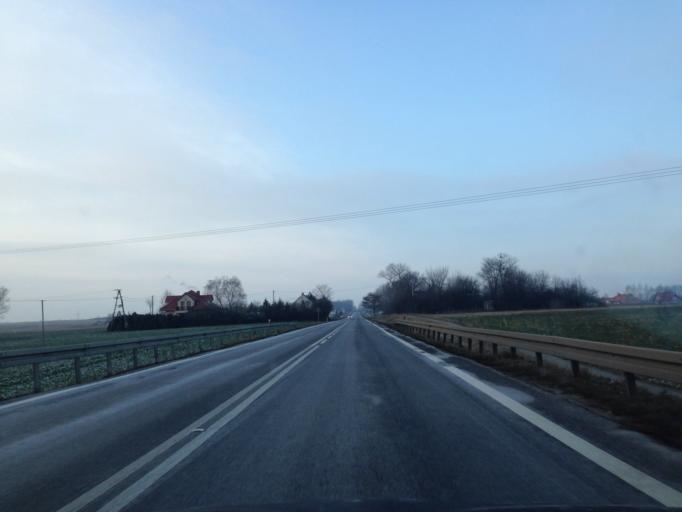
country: PL
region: Greater Poland Voivodeship
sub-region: Powiat poznanski
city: Pobiedziska
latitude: 52.5072
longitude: 17.3634
